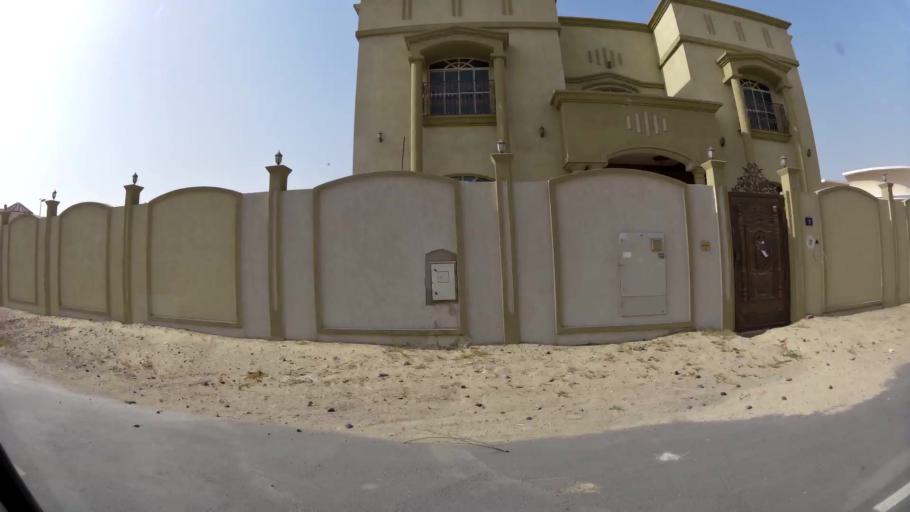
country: AE
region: Ash Shariqah
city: Sharjah
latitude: 25.2622
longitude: 55.4580
